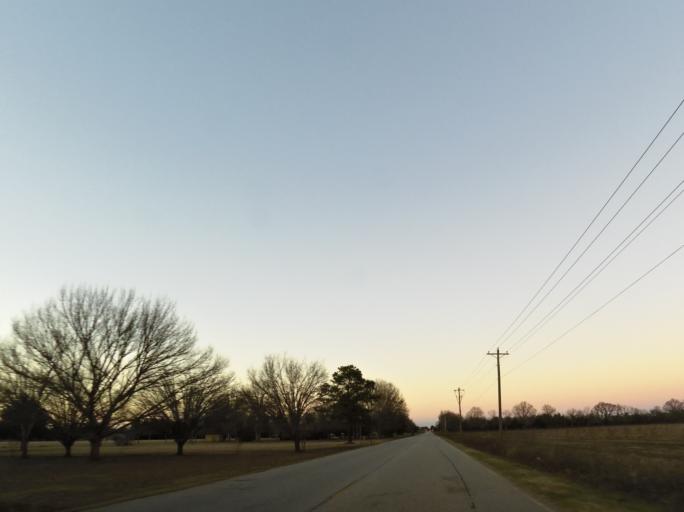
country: US
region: Georgia
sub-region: Peach County
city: Byron
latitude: 32.6005
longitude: -83.7481
